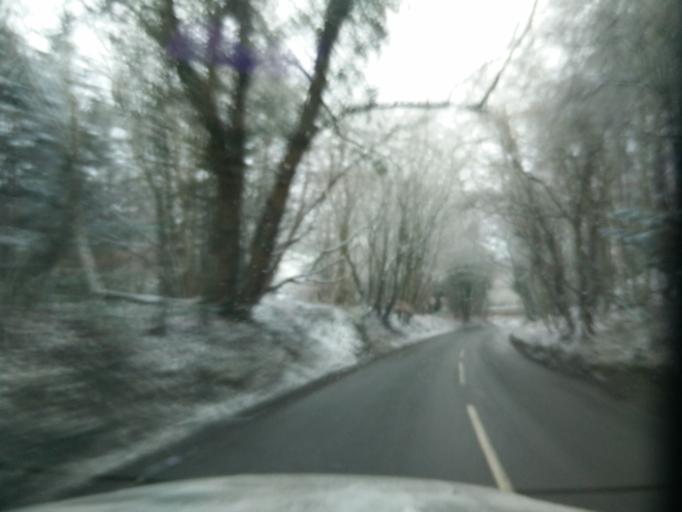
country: GB
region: England
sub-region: Buckinghamshire
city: Princes Risborough
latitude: 51.7330
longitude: -0.8036
